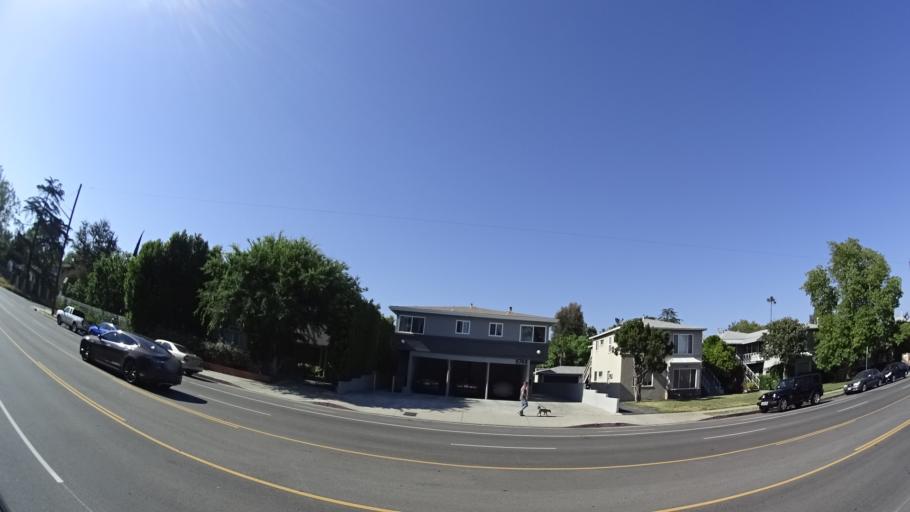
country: US
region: California
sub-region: Los Angeles County
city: North Hollywood
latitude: 34.1576
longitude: -118.3895
